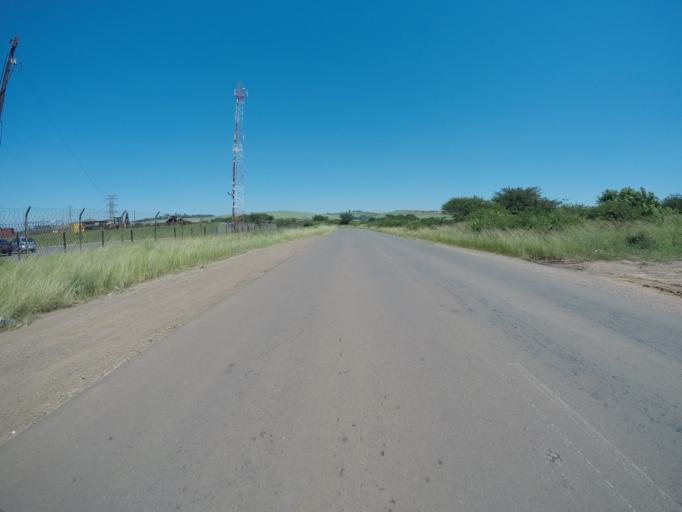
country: ZA
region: KwaZulu-Natal
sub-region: uThungulu District Municipality
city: Empangeni
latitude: -28.7208
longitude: 31.8679
